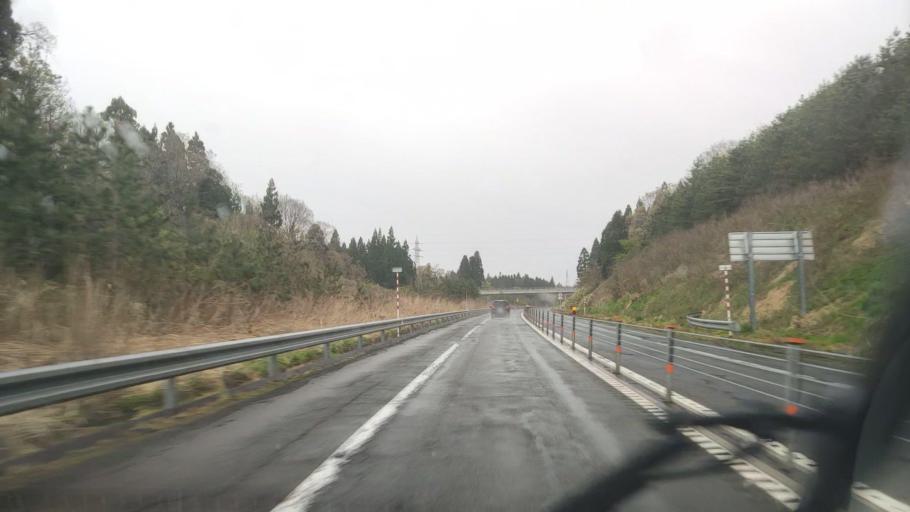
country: JP
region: Akita
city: Noshiromachi
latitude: 40.1694
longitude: 140.0518
